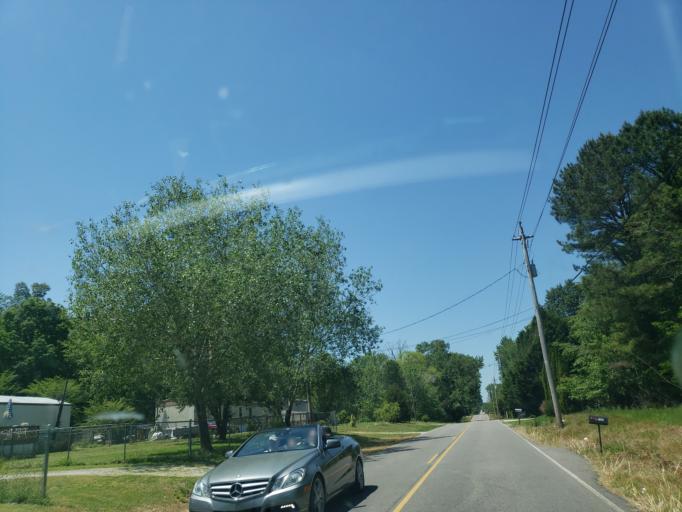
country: US
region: Alabama
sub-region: Madison County
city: Hazel Green
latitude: 34.9623
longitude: -86.6688
